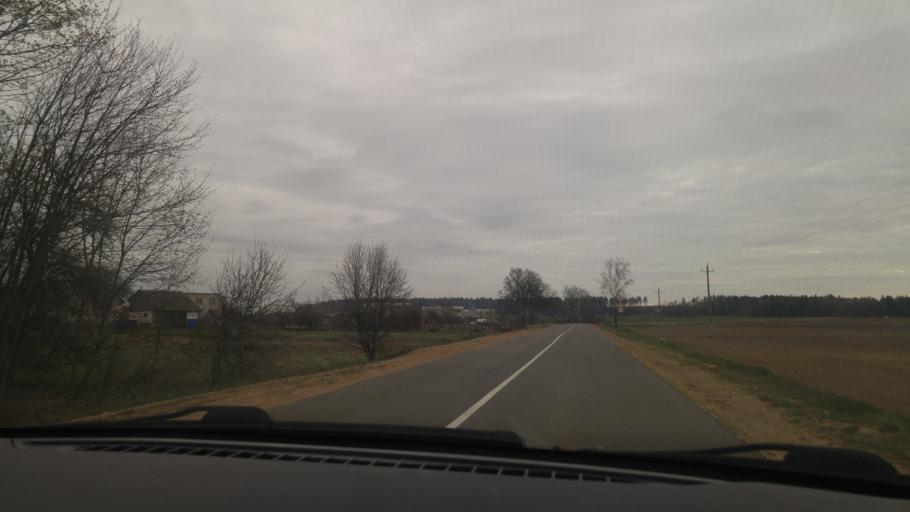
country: BY
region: Minsk
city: Chervyen'
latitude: 53.7297
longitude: 28.2762
